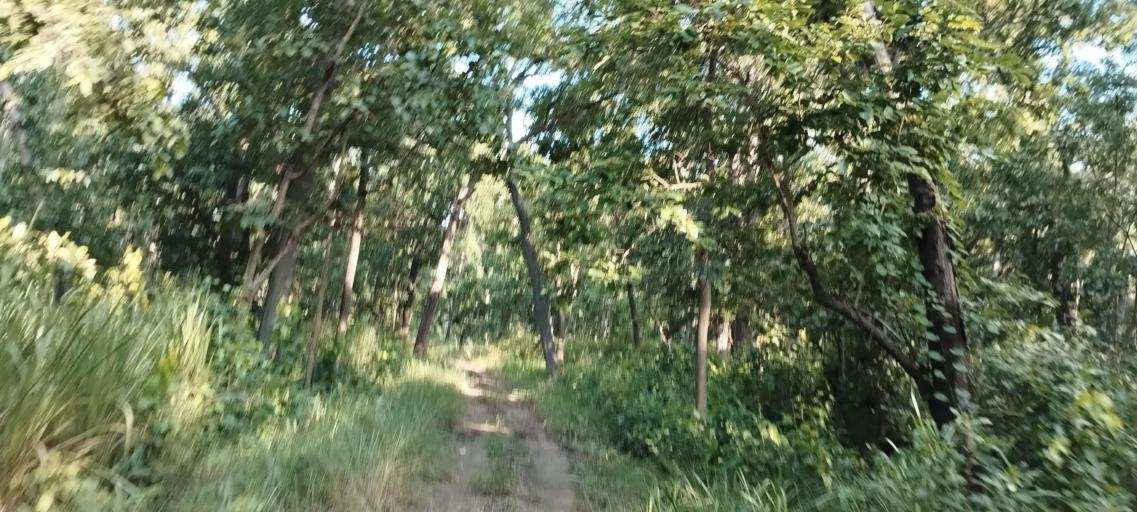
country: NP
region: Far Western
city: Tikapur
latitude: 28.5206
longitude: 81.2745
